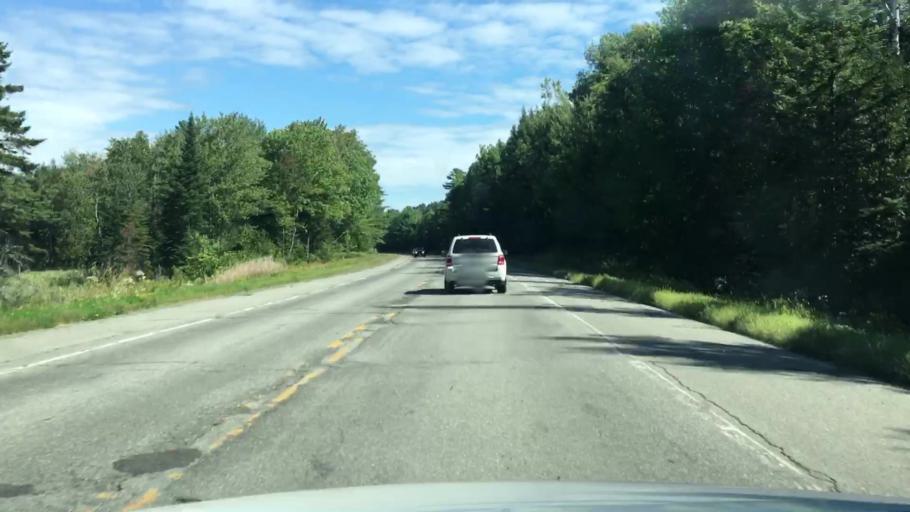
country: US
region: Maine
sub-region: Penobscot County
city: Dexter
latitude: 45.0516
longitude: -69.2614
